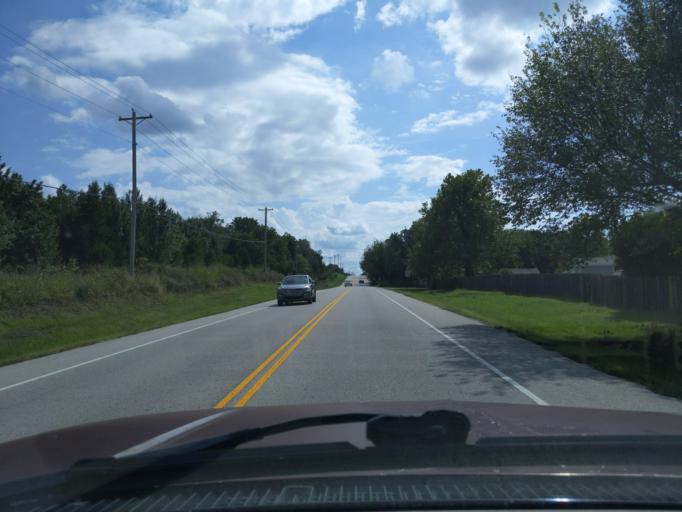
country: US
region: Oklahoma
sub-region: Tulsa County
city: Oakhurst
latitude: 36.0693
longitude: -96.0116
